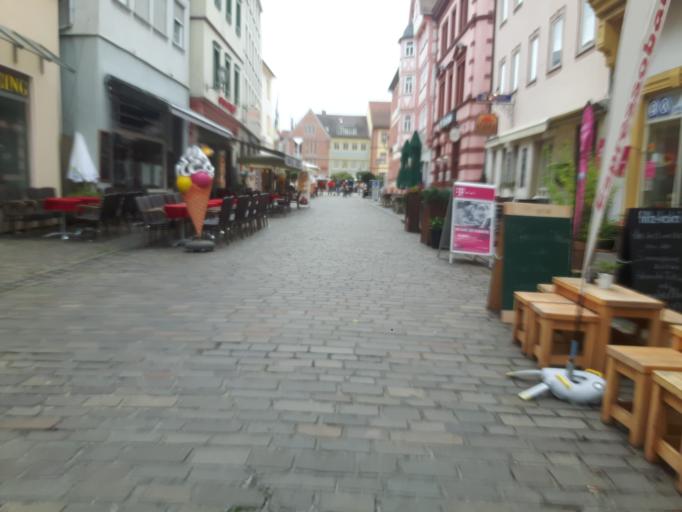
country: DE
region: Bavaria
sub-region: Regierungsbezirk Unterfranken
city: Karlstadt
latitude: 49.9622
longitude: 9.7642
